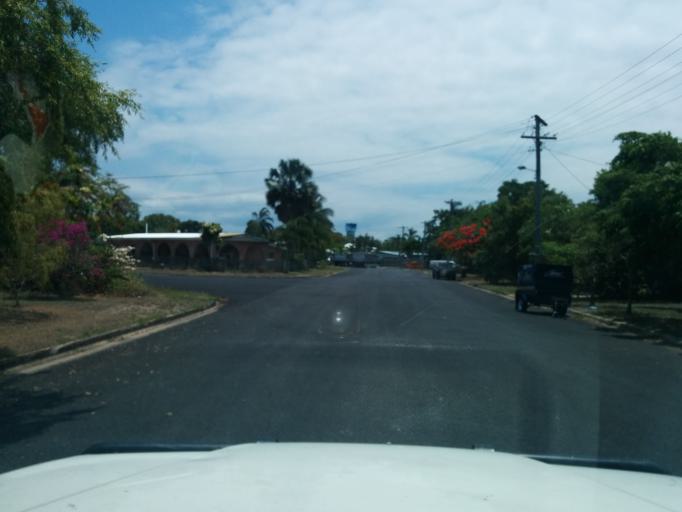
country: AU
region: Queensland
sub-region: Cairns
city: Yorkeys Knob
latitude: -16.8386
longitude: 145.7377
